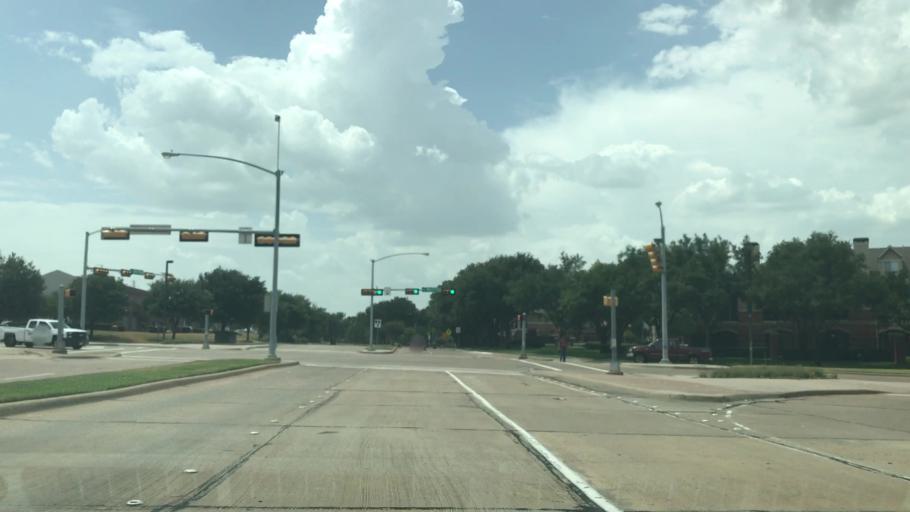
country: US
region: Texas
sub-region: Dallas County
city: Farmers Branch
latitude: 32.9233
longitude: -96.9549
